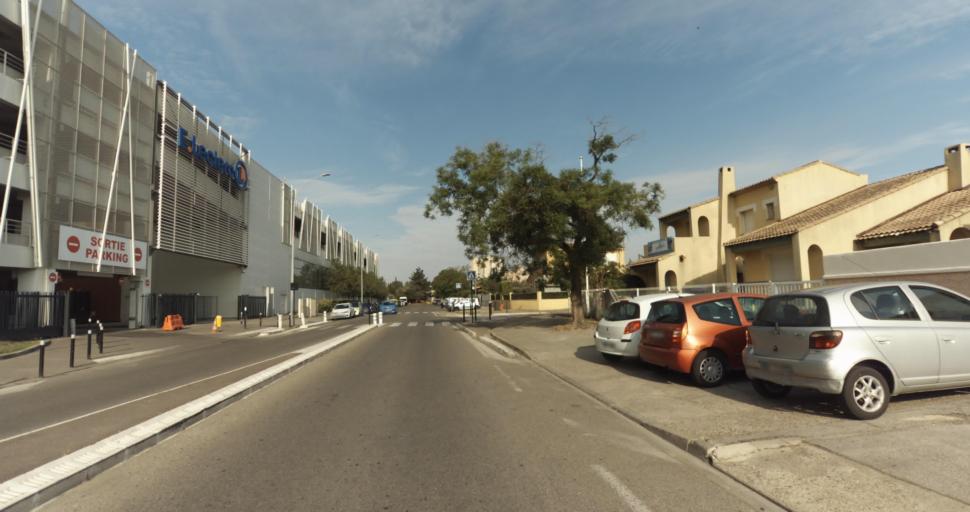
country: FR
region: Languedoc-Roussillon
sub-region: Departement du Gard
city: Rodilhan
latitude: 43.8373
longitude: 4.3938
